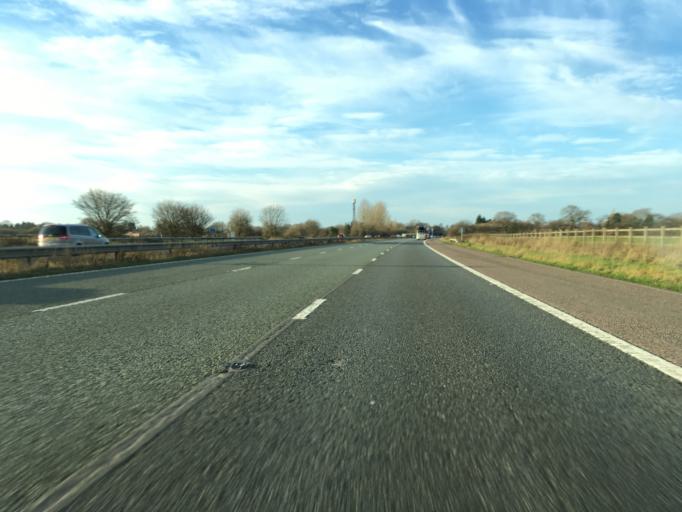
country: GB
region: England
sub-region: Warrington
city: Lymm
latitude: 53.3628
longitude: -2.4390
